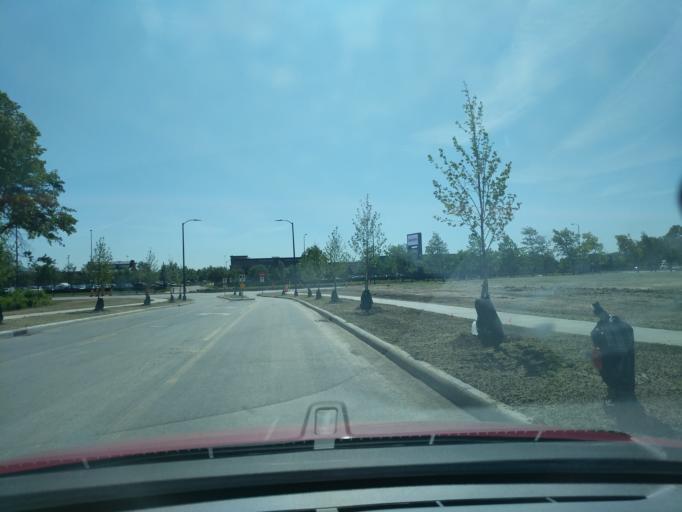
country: US
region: Ohio
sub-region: Franklin County
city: Huber Ridge
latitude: 40.0560
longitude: -82.9117
